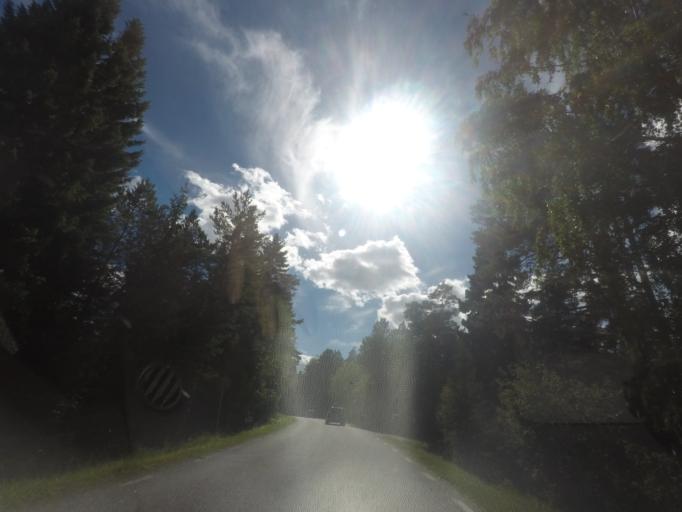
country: SE
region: Stockholm
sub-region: Norrtalje Kommun
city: Arno
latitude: 60.1461
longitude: 18.7810
